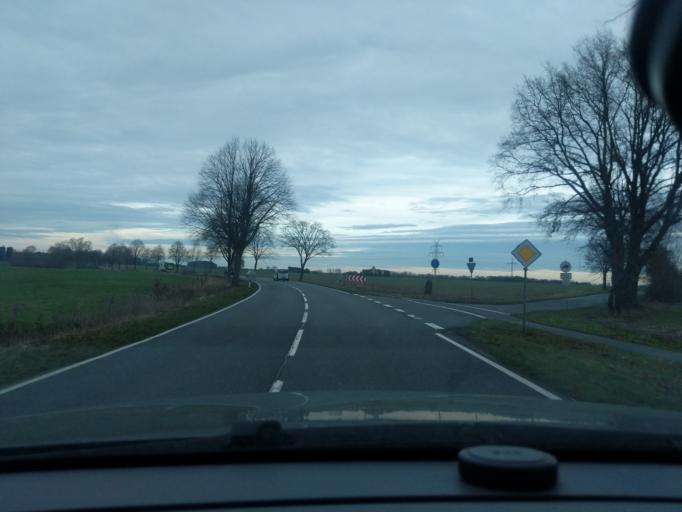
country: DE
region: Lower Saxony
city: Sauensiek
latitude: 53.3964
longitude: 9.6094
